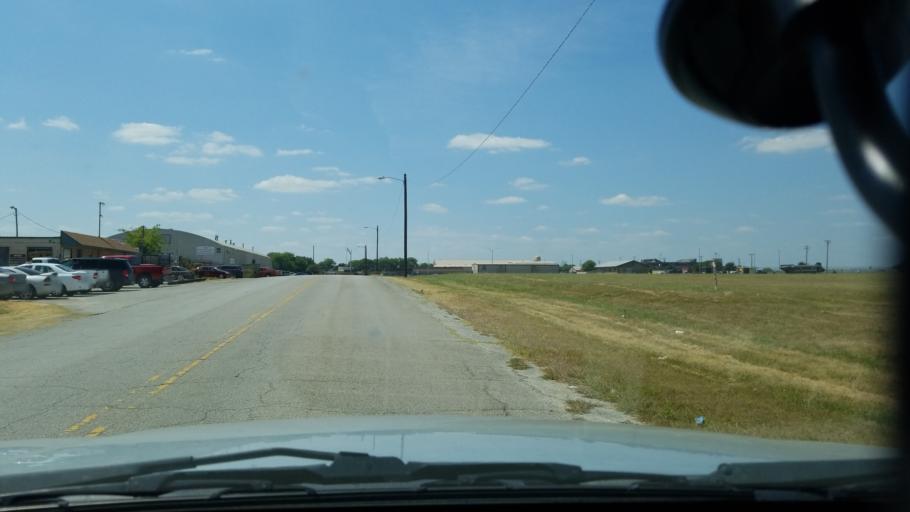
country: US
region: Texas
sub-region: Dallas County
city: Grand Prairie
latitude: 32.7440
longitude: -96.9580
